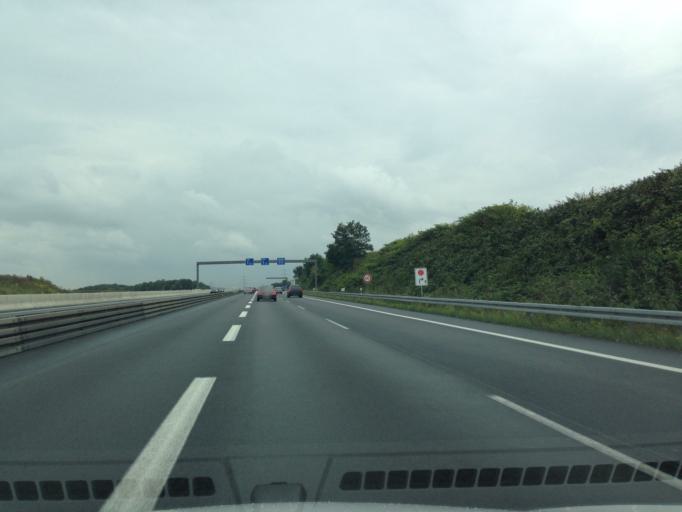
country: DE
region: North Rhine-Westphalia
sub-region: Regierungsbezirk Dusseldorf
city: Kaarst
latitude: 51.2403
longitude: 6.6376
